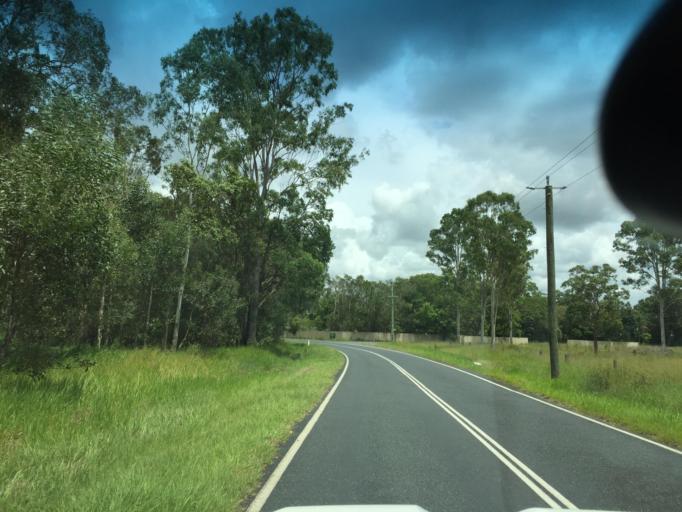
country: AU
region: Queensland
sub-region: Moreton Bay
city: Caboolture
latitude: -27.0462
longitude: 152.9131
